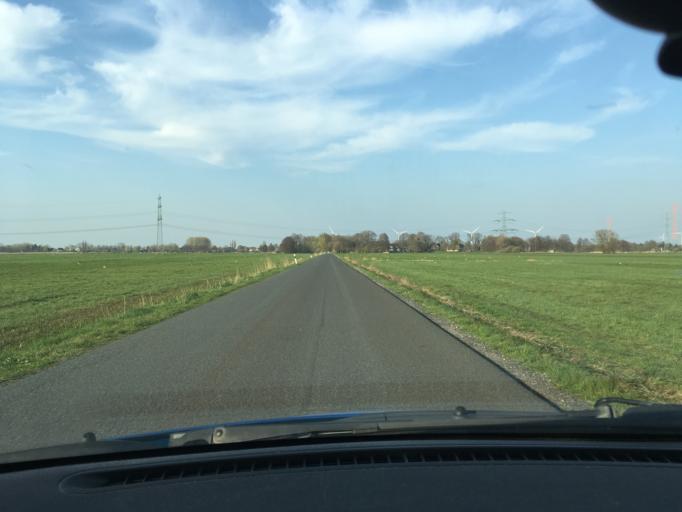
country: DE
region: Lower Saxony
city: Stelle
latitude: 53.4405
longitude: 10.0596
